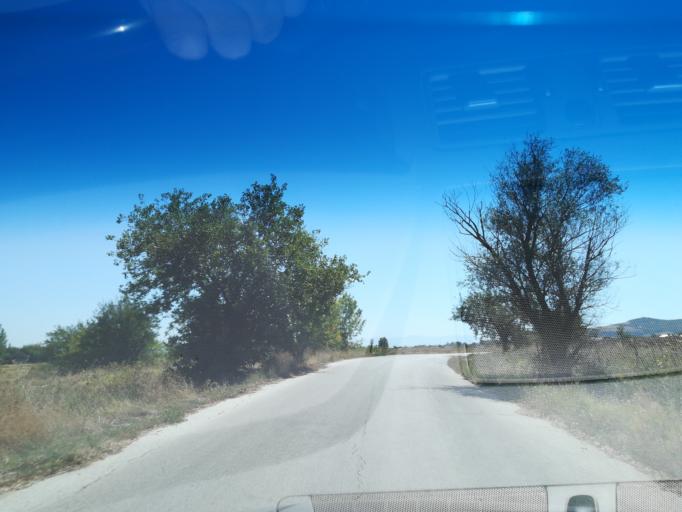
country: BG
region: Pazardzhik
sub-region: Obshtina Strelcha
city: Strelcha
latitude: 42.3562
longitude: 24.3996
